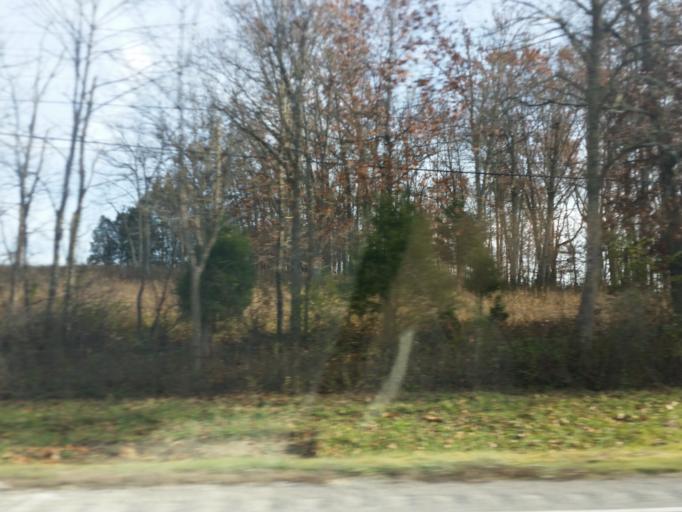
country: US
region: Kentucky
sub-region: Pendleton County
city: Falmouth
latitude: 38.7486
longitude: -84.3583
